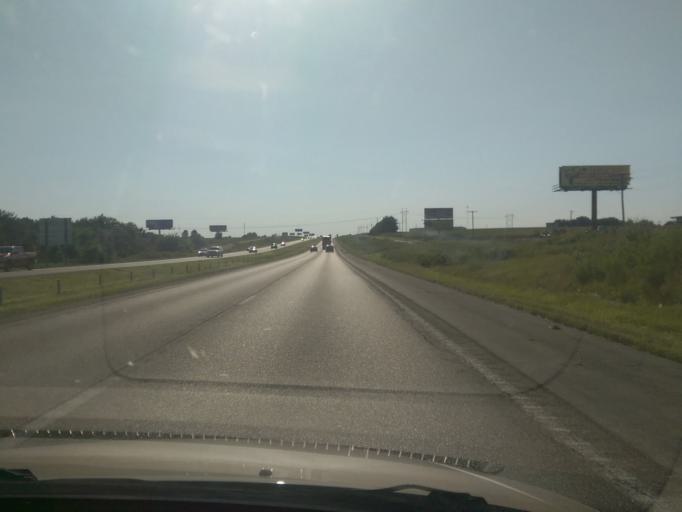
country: US
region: Missouri
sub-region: Lafayette County
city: Higginsville
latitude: 39.0011
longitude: -93.7437
